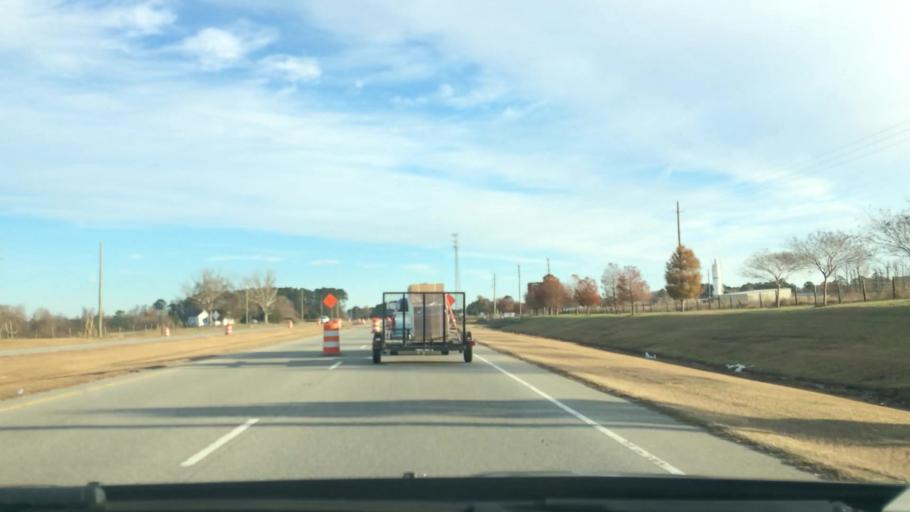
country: US
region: North Carolina
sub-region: Pitt County
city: Winterville
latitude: 35.5151
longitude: -77.4129
